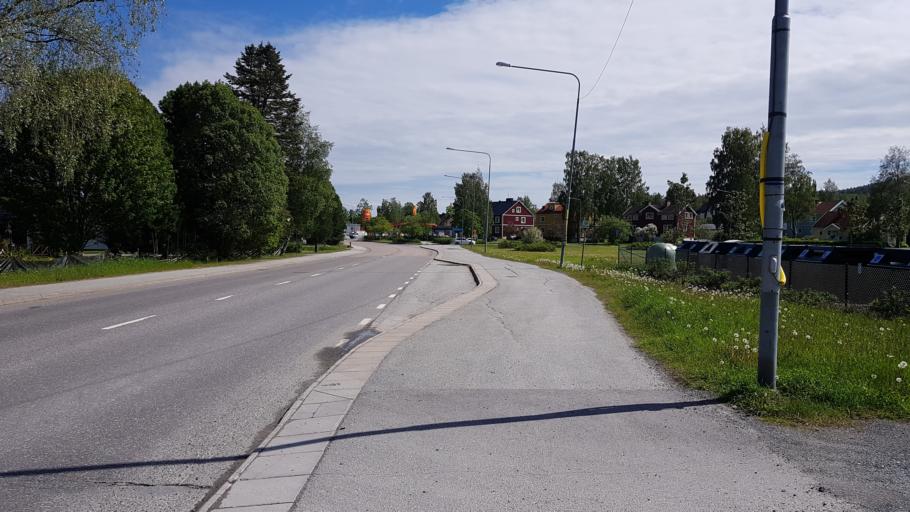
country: SE
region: Vaesternorrland
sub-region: OErnskoeldsviks Kommun
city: Ornskoldsvik
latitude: 63.3164
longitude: 18.6937
